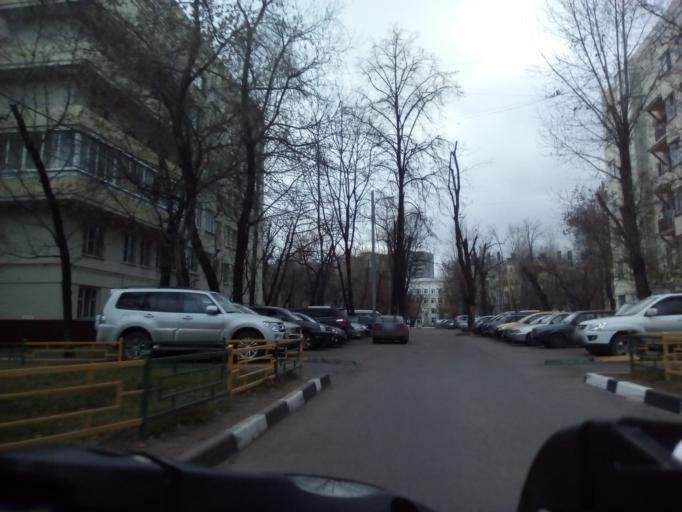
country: RU
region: Moscow
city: Lefortovo
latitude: 55.7468
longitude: 37.7181
